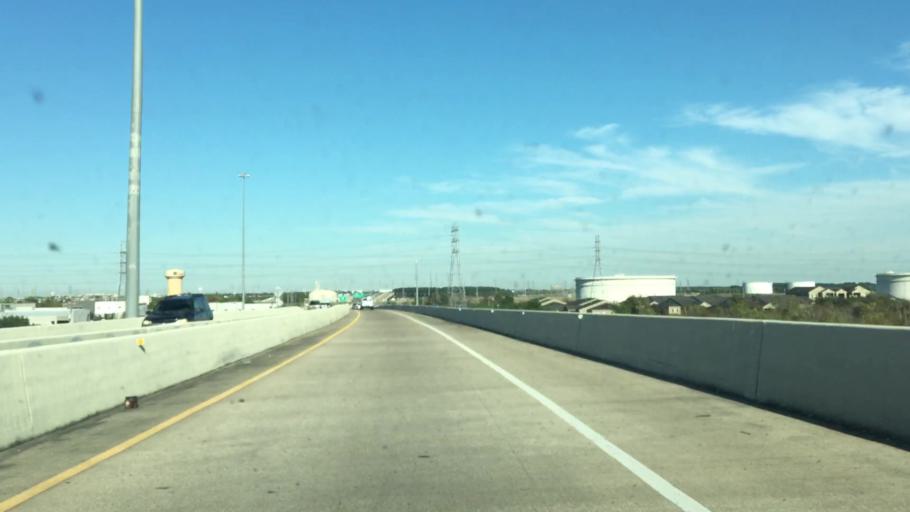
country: US
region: Texas
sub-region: Harris County
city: Webster
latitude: 29.5228
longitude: -95.1222
